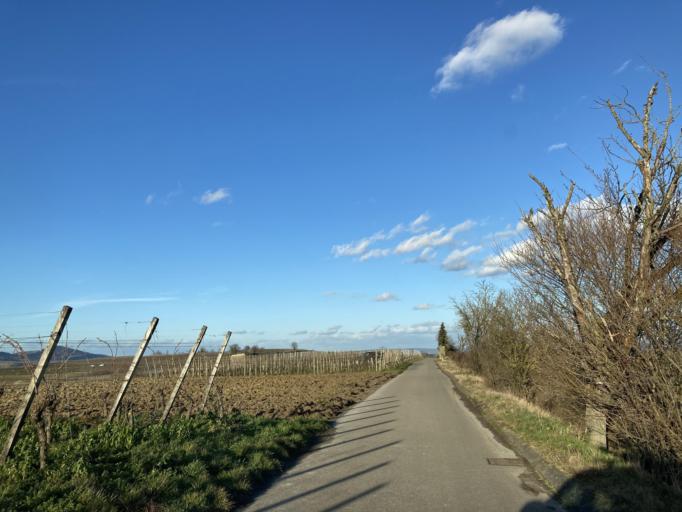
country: DE
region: Baden-Wuerttemberg
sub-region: Freiburg Region
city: Merdingen
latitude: 48.0098
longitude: 7.6957
